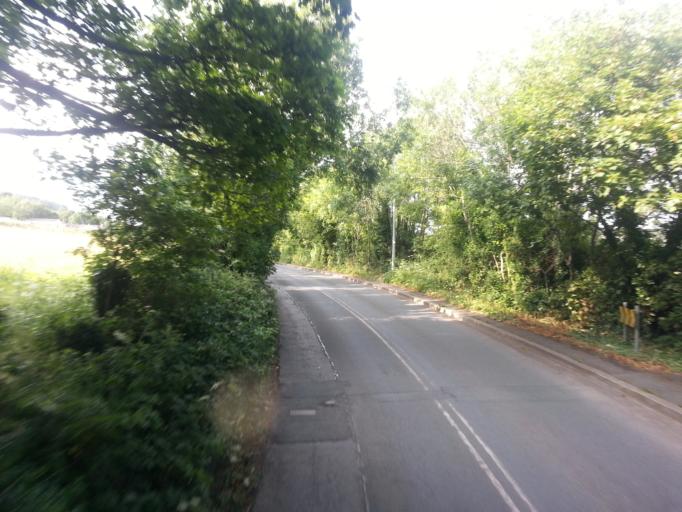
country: IE
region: Leinster
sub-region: Wicklow
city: Enniskerry
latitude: 53.2068
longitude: -6.1742
